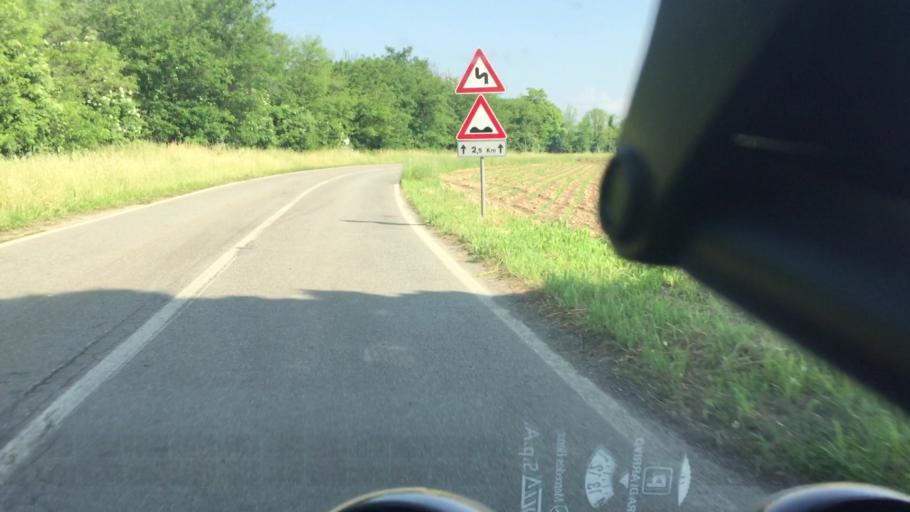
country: IT
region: Lombardy
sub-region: Provincia di Bergamo
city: Badalasco
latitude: 45.5500
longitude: 9.5666
